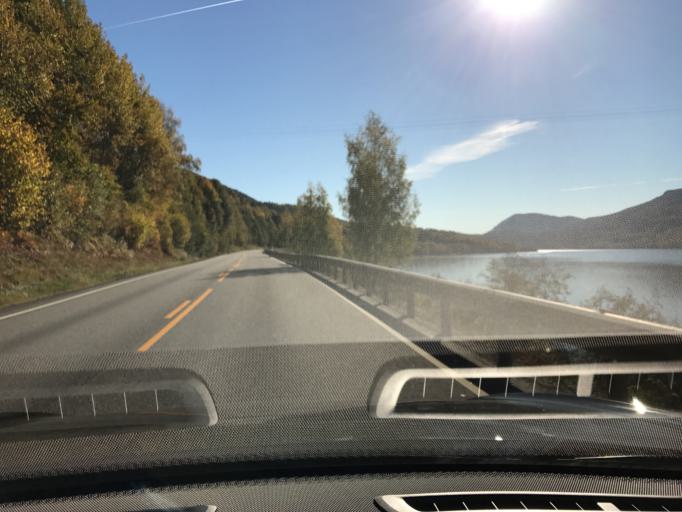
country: NO
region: Buskerud
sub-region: Krodsherad
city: Noresund
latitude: 60.3637
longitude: 9.6421
